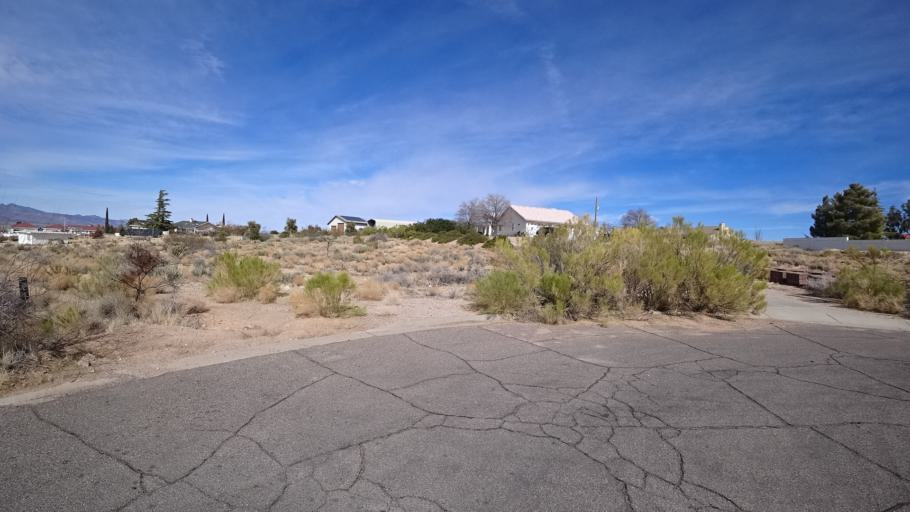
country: US
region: Arizona
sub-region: Mohave County
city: Kingman
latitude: 35.1879
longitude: -113.9911
